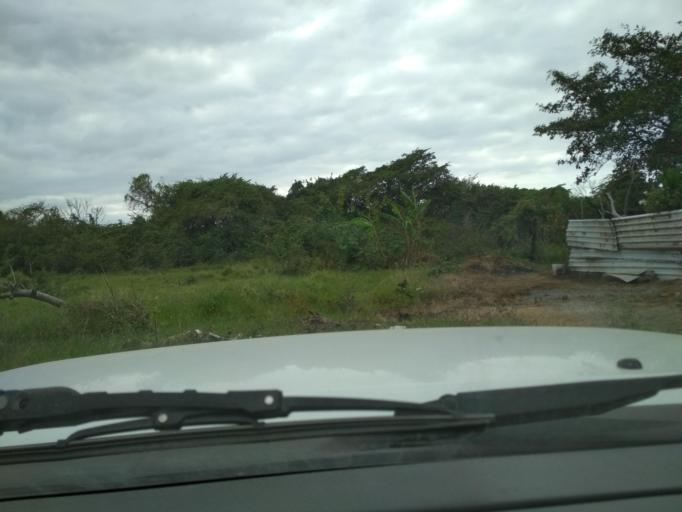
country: MX
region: Veracruz
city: El Tejar
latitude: 19.0717
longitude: -96.1477
